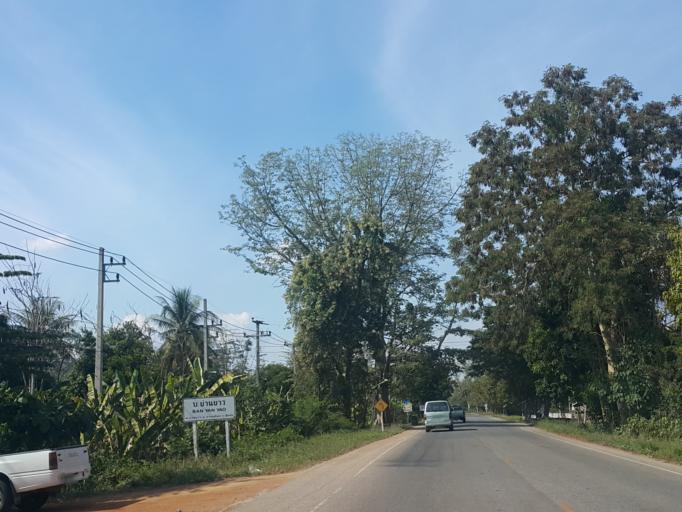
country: TH
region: Sukhothai
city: Sawankhalok
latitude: 17.2520
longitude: 99.8441
